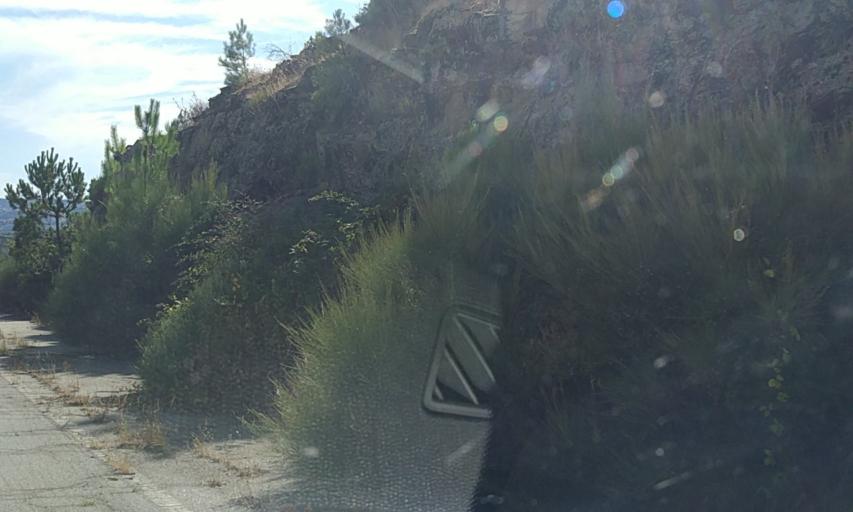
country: PT
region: Vila Real
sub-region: Sabrosa
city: Sabrosa
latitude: 41.3639
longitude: -7.5555
